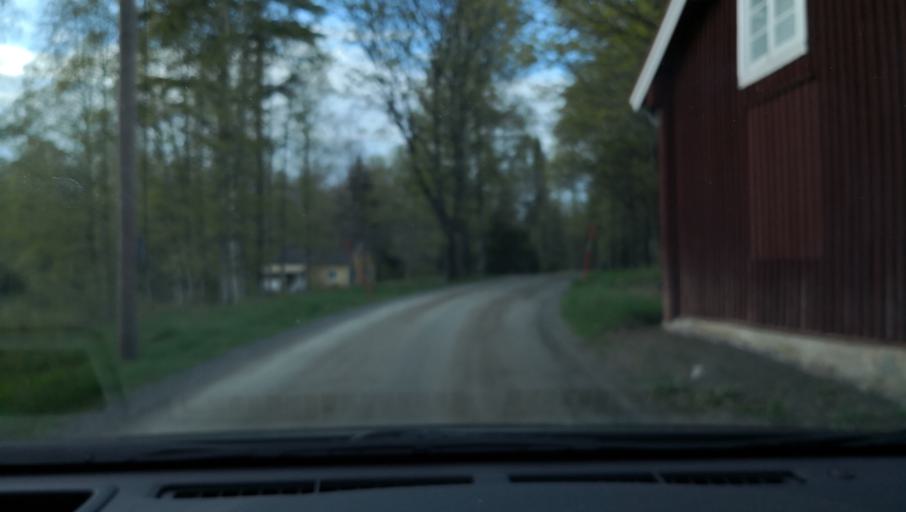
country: SE
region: Dalarna
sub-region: Saters Kommun
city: Saeter
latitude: 60.2656
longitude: 15.8280
